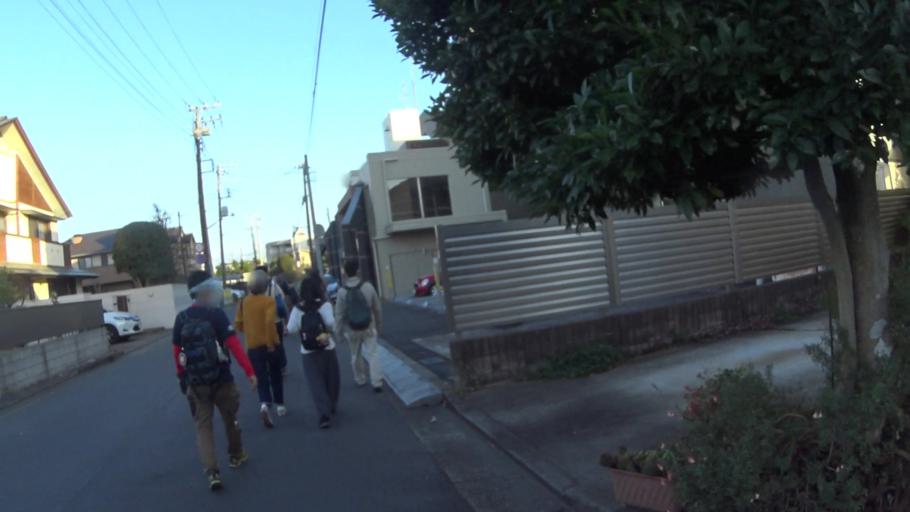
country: JP
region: Ibaraki
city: Mito-shi
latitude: 36.3735
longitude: 140.4623
